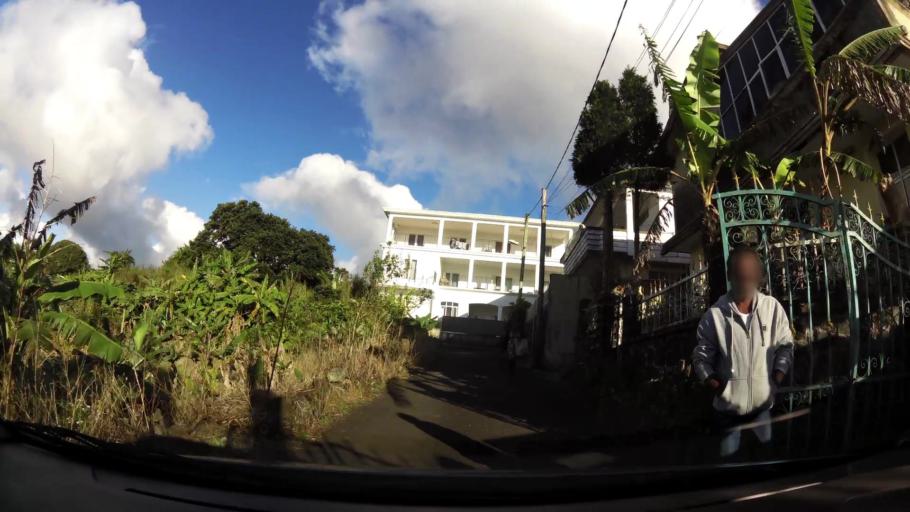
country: MU
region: Plaines Wilhems
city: Curepipe
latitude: -20.3156
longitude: 57.5127
